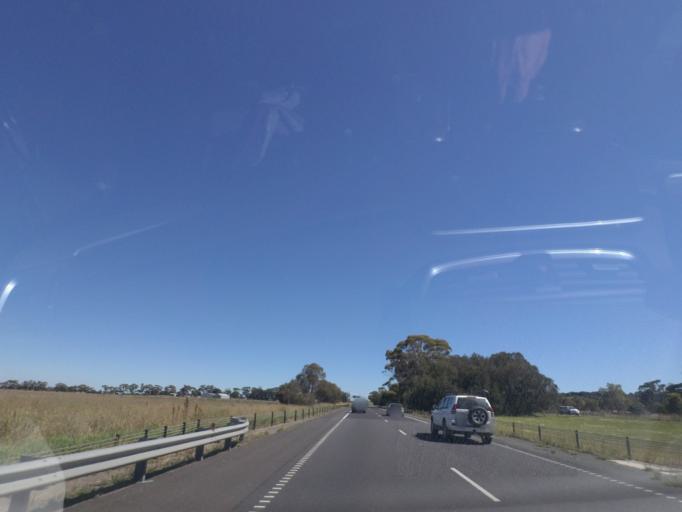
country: AU
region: Victoria
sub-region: Hume
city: Craigieburn
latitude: -37.5578
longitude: 144.9429
